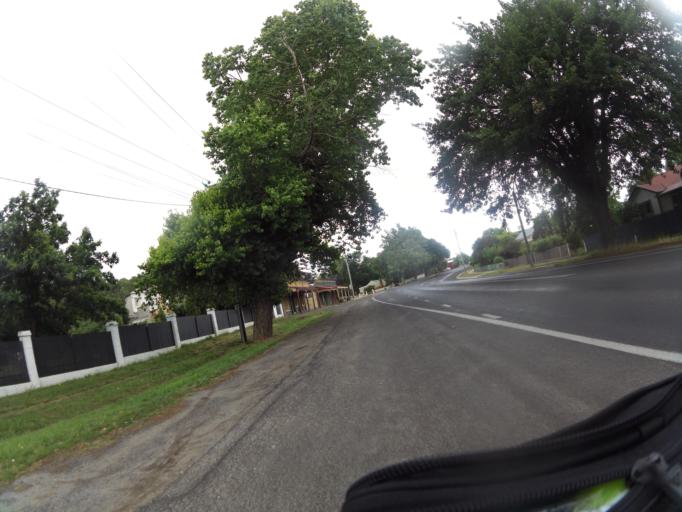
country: AU
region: Victoria
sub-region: Mount Alexander
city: Castlemaine
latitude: -37.0706
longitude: 144.2112
